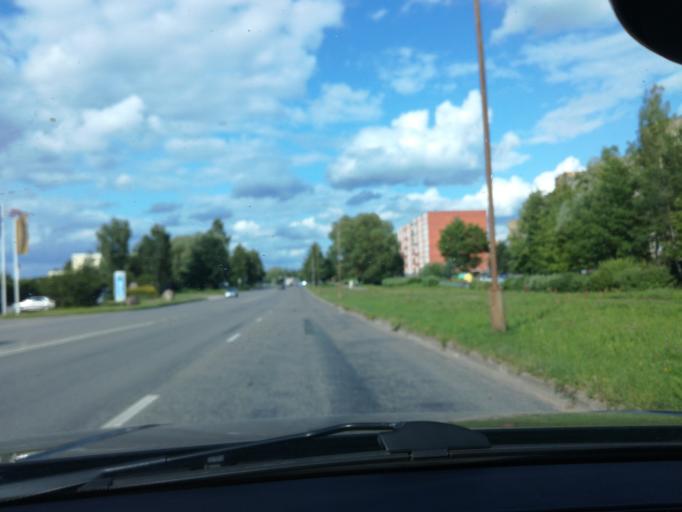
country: LT
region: Alytaus apskritis
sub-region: Alytus
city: Alytus
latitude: 54.4106
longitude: 24.0079
